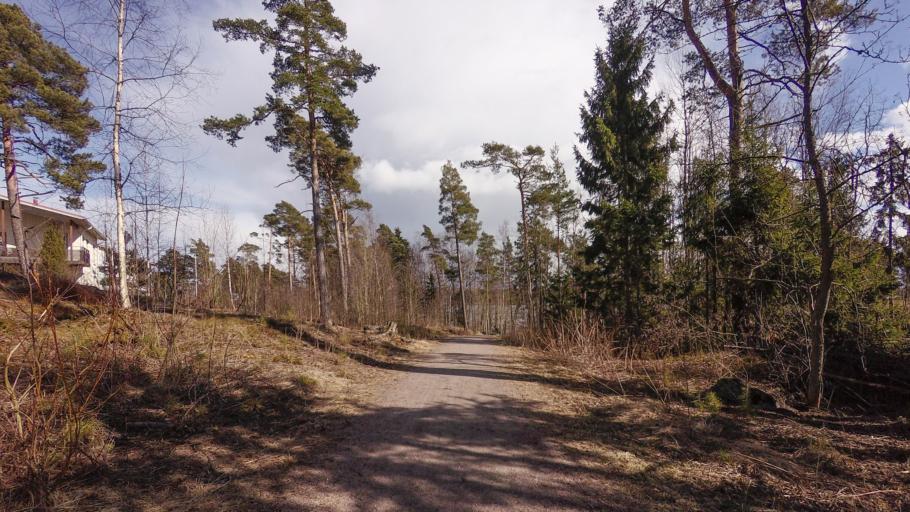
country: FI
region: Uusimaa
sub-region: Helsinki
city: Vantaa
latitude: 60.1967
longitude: 25.1217
